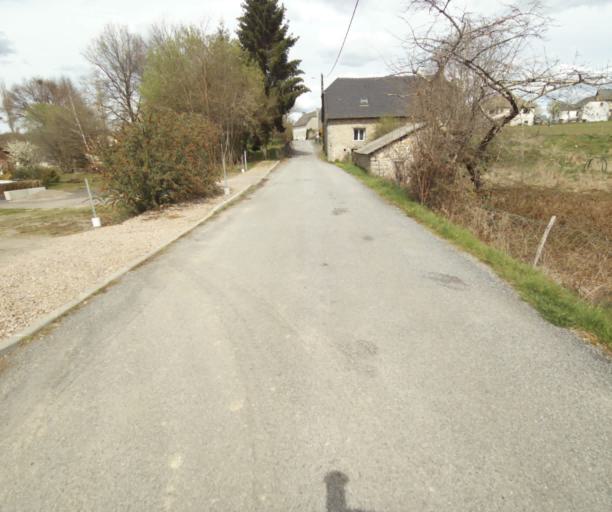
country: FR
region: Limousin
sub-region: Departement de la Correze
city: Laguenne
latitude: 45.2178
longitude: 1.8947
